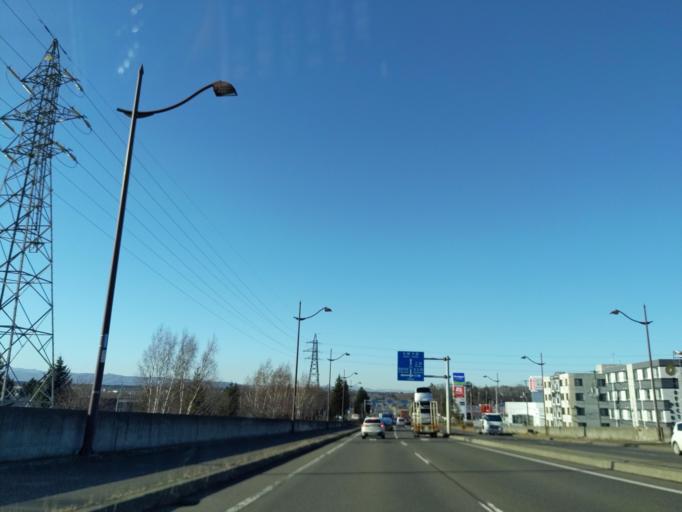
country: JP
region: Hokkaido
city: Kitahiroshima
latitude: 42.9011
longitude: 141.5730
